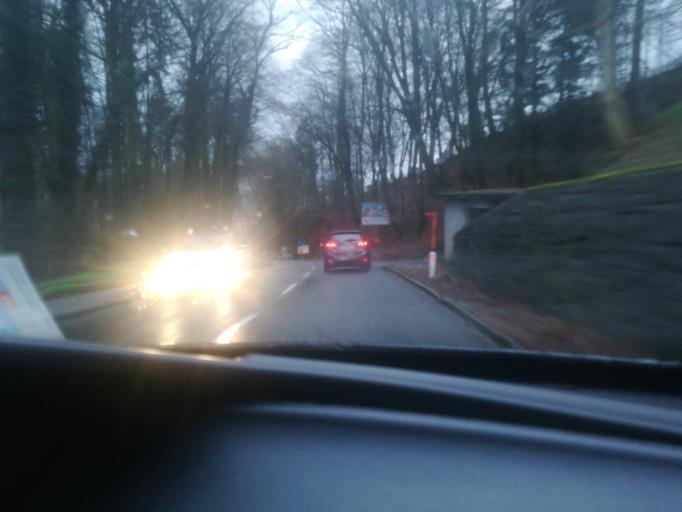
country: AT
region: Upper Austria
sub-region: Politischer Bezirk Perg
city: Perg
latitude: 48.2535
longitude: 14.6284
